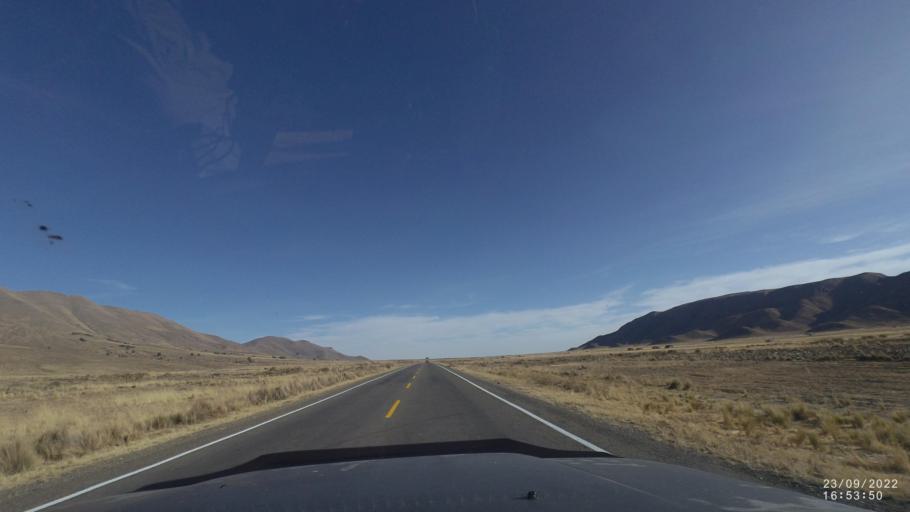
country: BO
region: Oruro
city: Poopo
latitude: -18.4539
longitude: -66.9709
